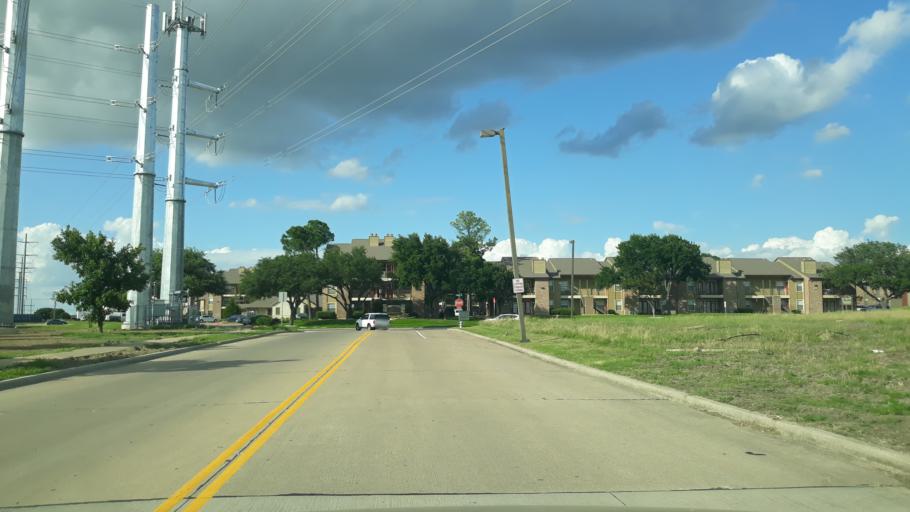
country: US
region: Texas
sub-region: Tarrant County
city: Euless
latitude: 32.8607
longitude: -97.0132
